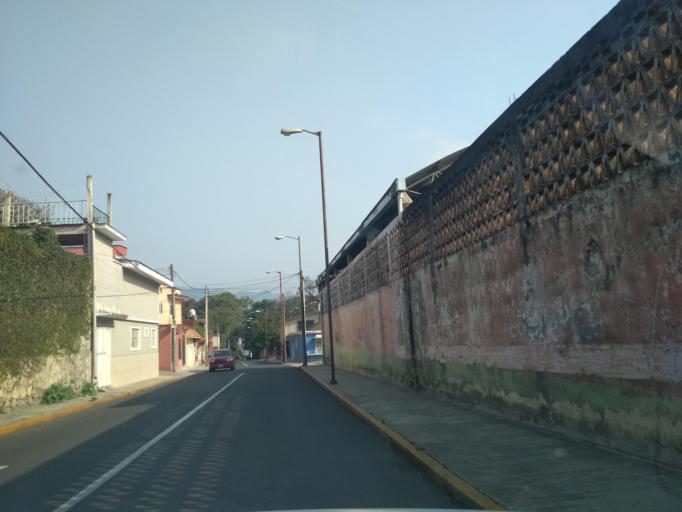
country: MX
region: Veracruz
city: Orizaba
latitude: 18.8570
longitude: -97.0919
